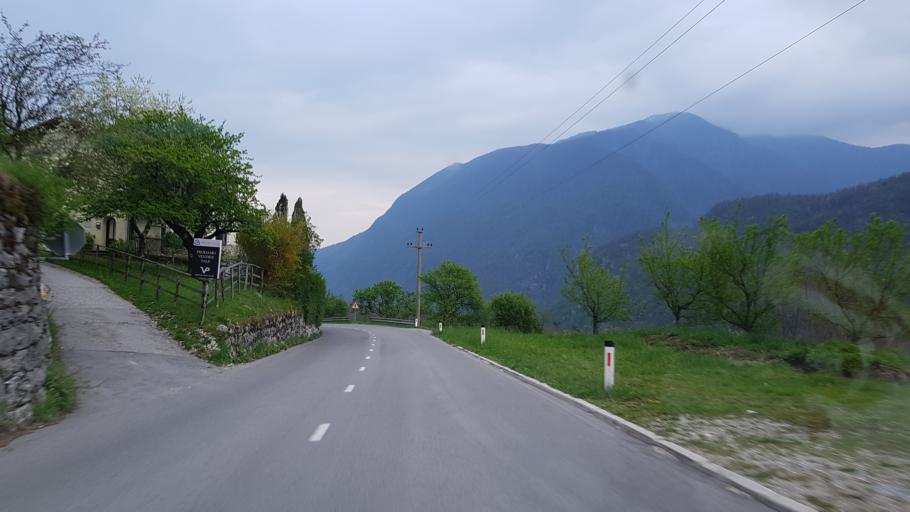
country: IT
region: Friuli Venezia Giulia
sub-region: Provincia di Udine
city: Pulfero
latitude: 46.2558
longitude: 13.4887
